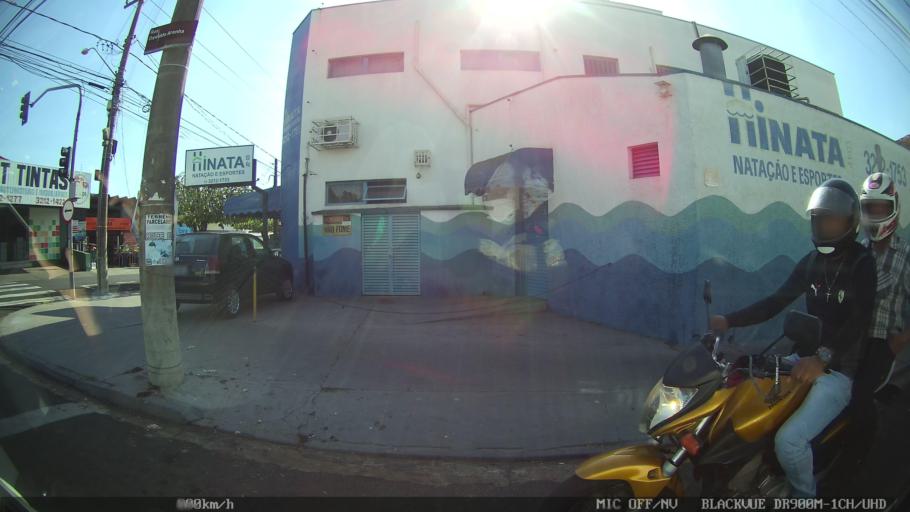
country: BR
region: Sao Paulo
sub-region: Sao Jose Do Rio Preto
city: Sao Jose do Rio Preto
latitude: -20.8035
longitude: -49.3929
